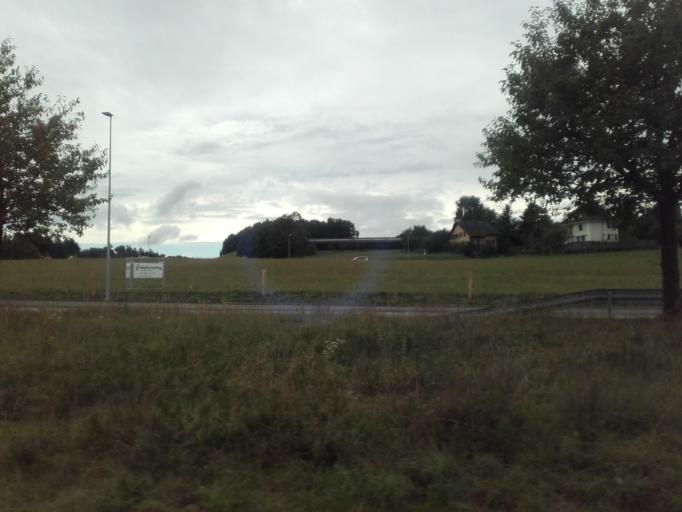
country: CH
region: Solothurn
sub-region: Bezirk Solothurn
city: Solothurn
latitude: 47.1976
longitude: 7.5476
